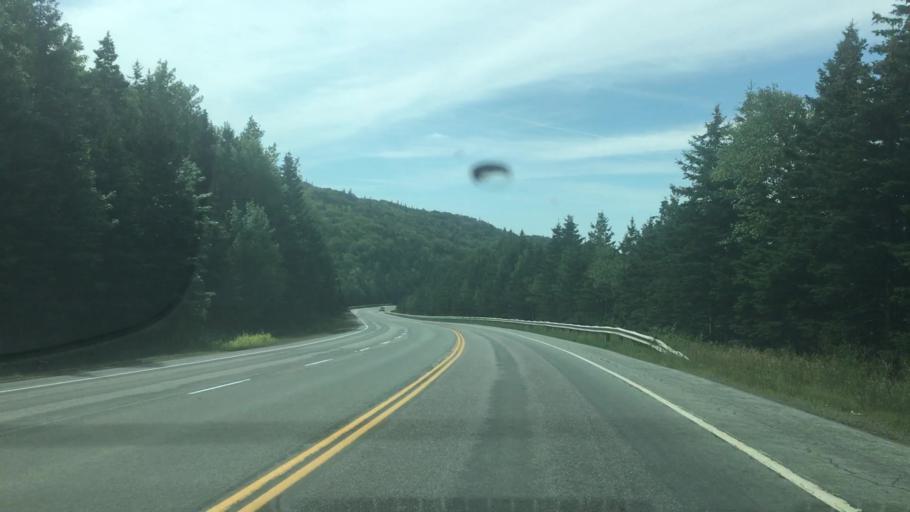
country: CA
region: Nova Scotia
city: Sydney Mines
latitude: 46.2434
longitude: -60.5592
